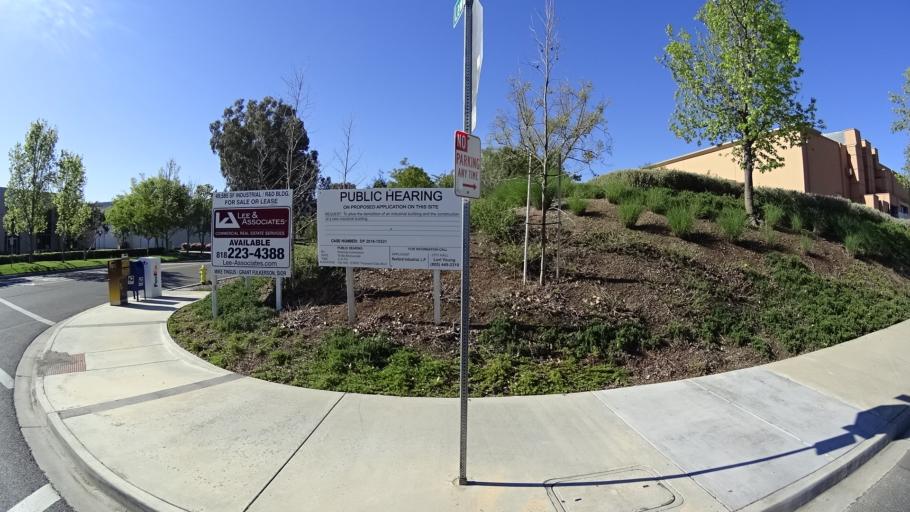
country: US
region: California
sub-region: Ventura County
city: Casa Conejo
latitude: 34.1898
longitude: -118.9301
